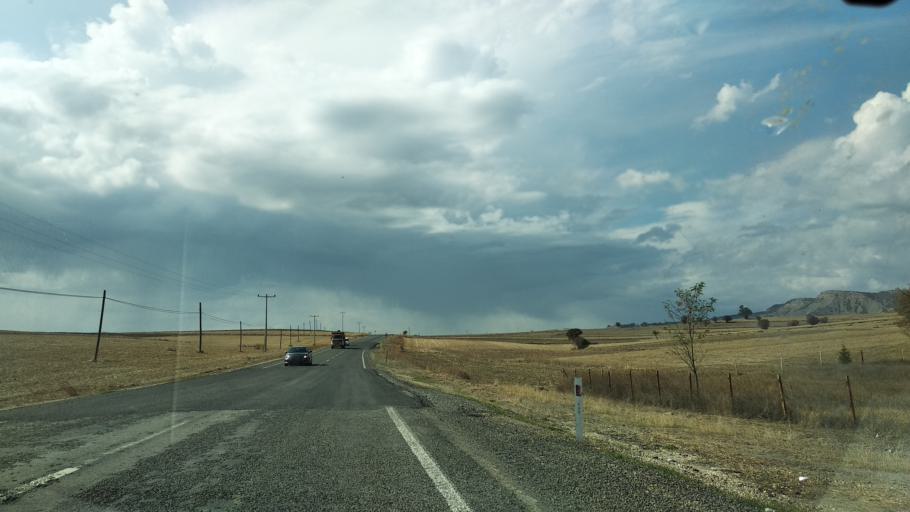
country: TR
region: Bolu
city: Seben
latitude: 40.3961
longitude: 31.5550
